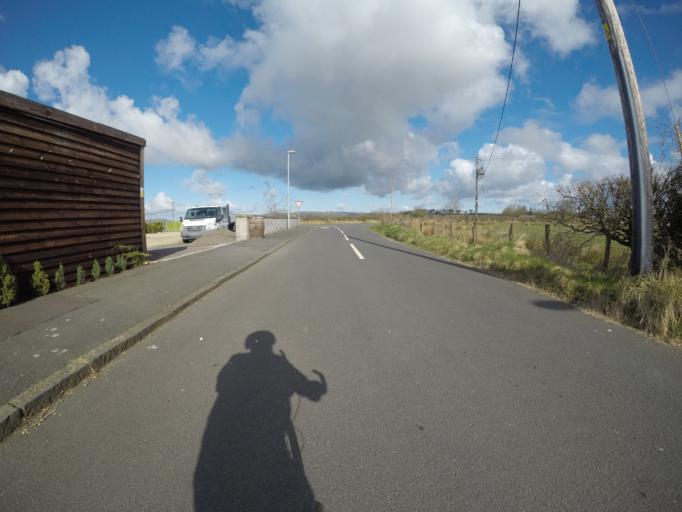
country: GB
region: Scotland
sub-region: North Ayrshire
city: Kilwinning
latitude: 55.6739
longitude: -4.6594
